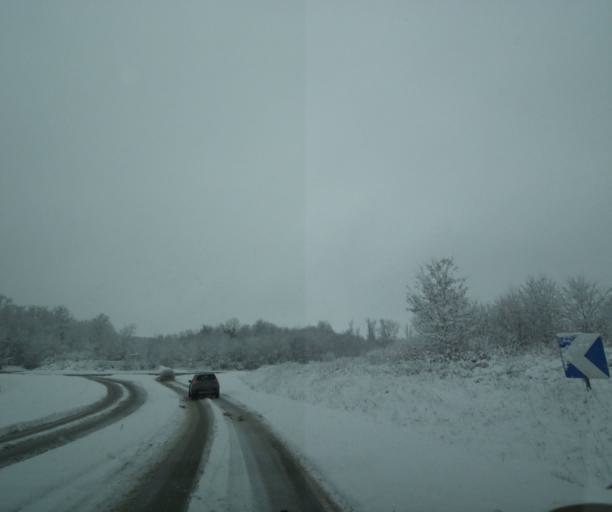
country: FR
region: Champagne-Ardenne
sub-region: Departement de la Haute-Marne
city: Saint-Dizier
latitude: 48.6047
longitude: 4.9109
